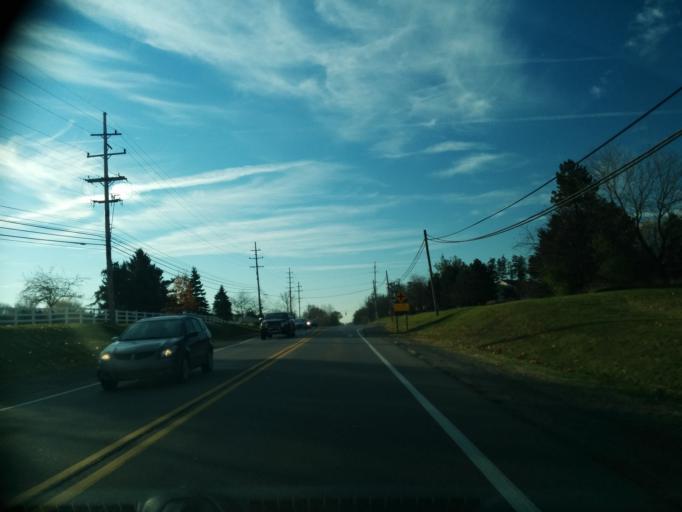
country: US
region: Michigan
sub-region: Oakland County
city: Farmington Hills
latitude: 42.4853
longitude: -83.4166
